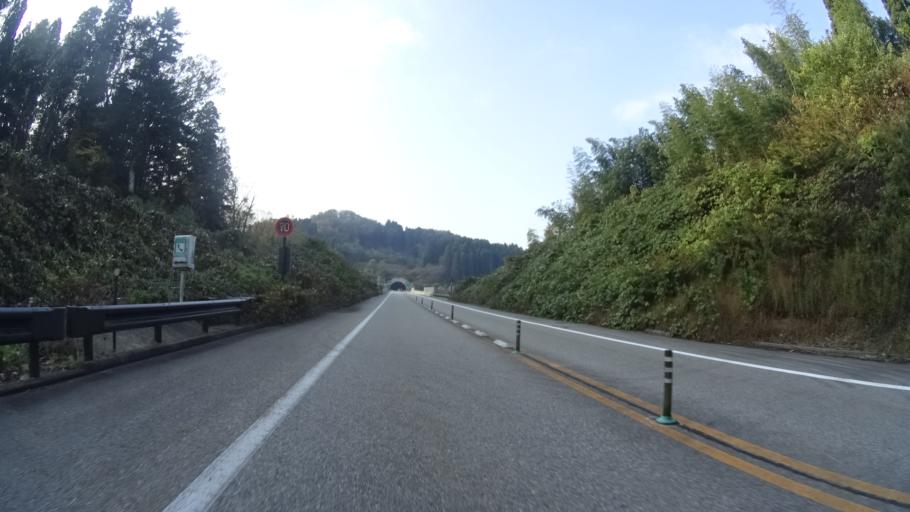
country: JP
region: Toyama
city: Himi
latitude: 36.8957
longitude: 136.9860
